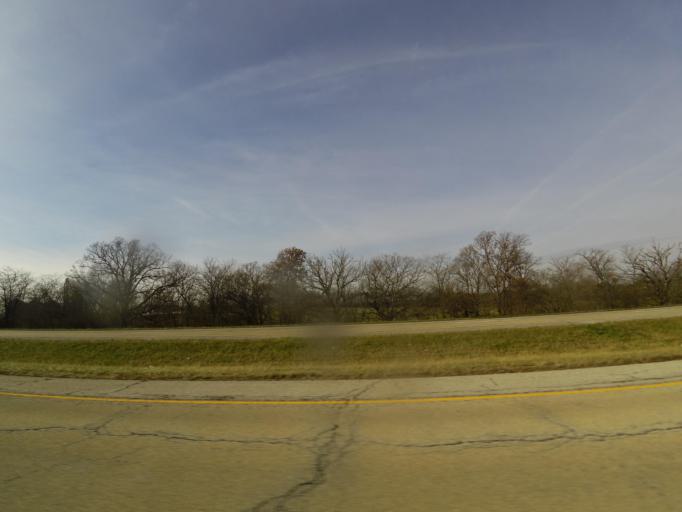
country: US
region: Illinois
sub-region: Macon County
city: Maroa
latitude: 40.0936
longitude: -88.9655
